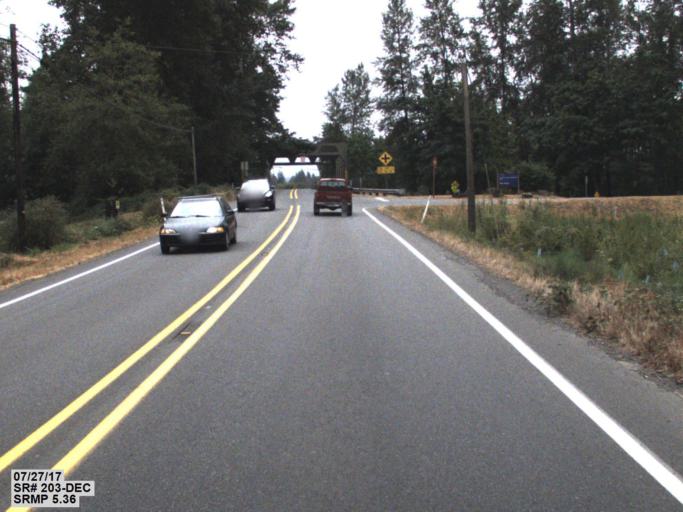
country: US
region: Washington
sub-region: King County
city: Carnation
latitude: 47.6394
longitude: -121.9163
